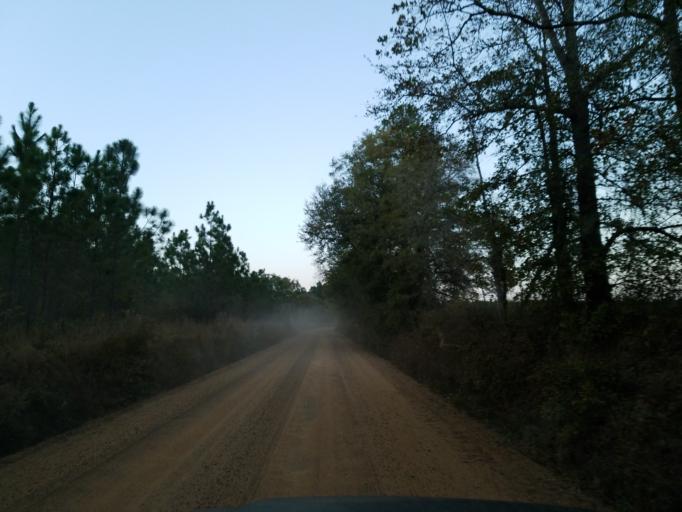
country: US
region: Georgia
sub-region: Turner County
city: Ashburn
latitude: 31.7327
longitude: -83.4841
